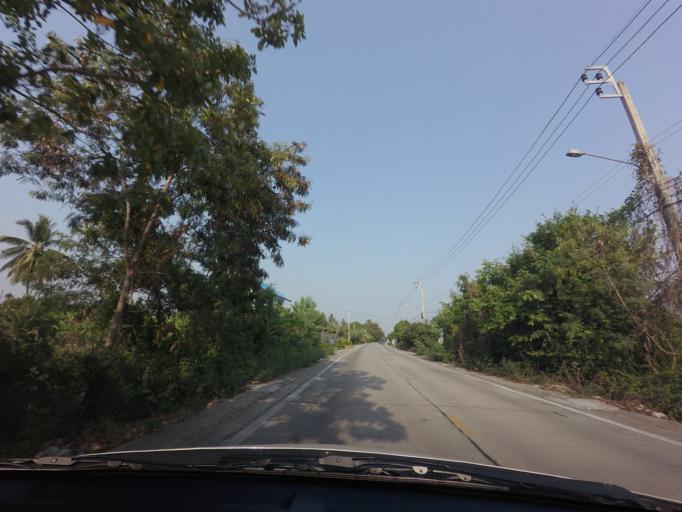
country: TH
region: Nonthaburi
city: Bang Yai
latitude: 13.8037
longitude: 100.3815
